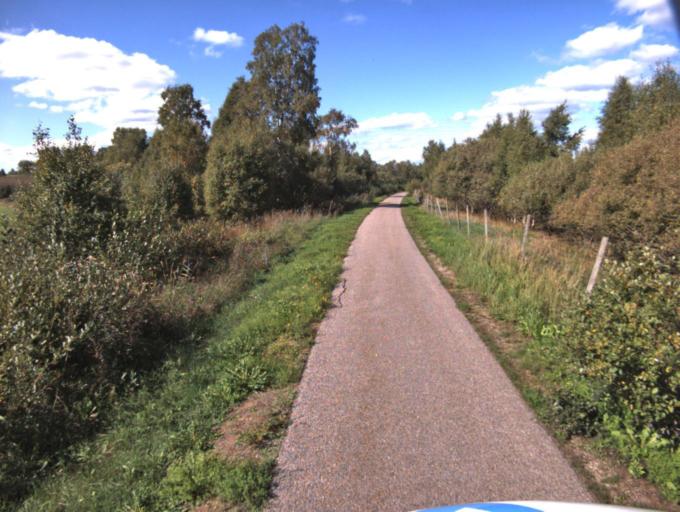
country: SE
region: Vaestra Goetaland
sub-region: Ulricehamns Kommun
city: Ulricehamn
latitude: 57.8400
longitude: 13.3043
